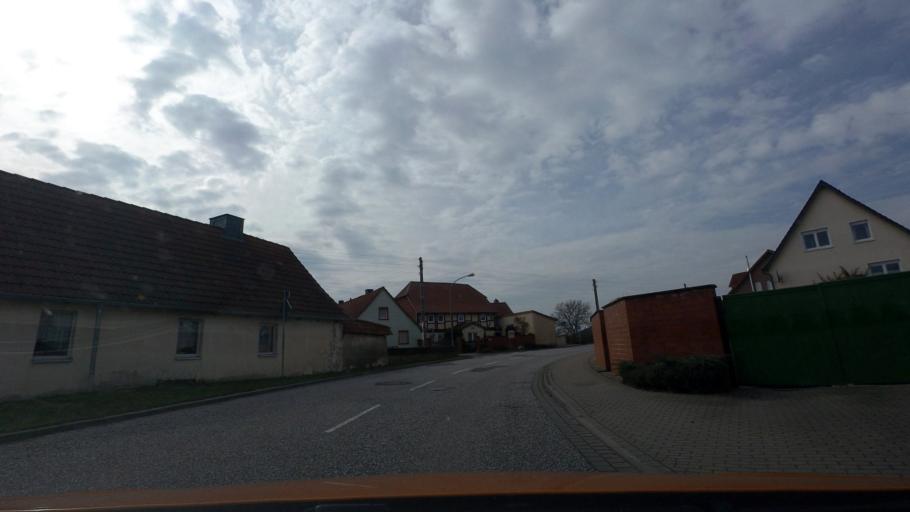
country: DE
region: Saxony-Anhalt
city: Erxleben
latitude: 52.2193
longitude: 11.2338
